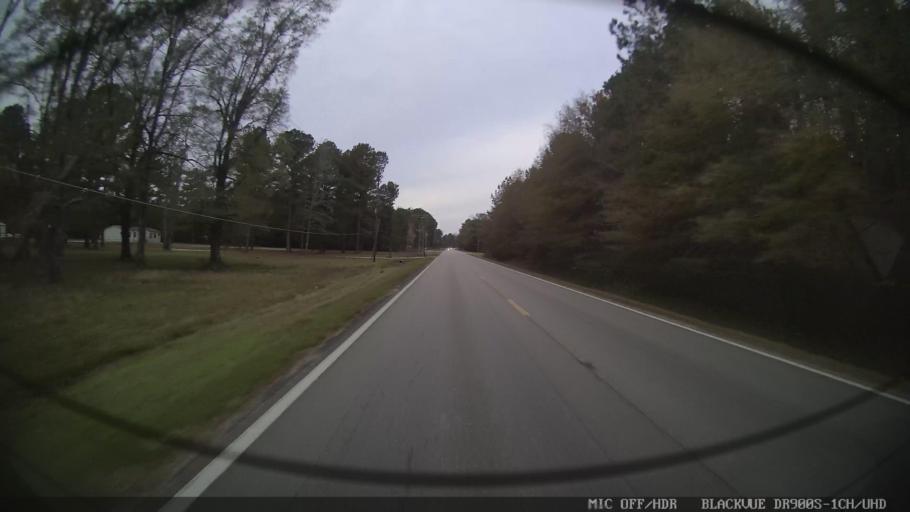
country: US
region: Mississippi
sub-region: Clarke County
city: Stonewall
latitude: 32.0257
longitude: -88.8576
